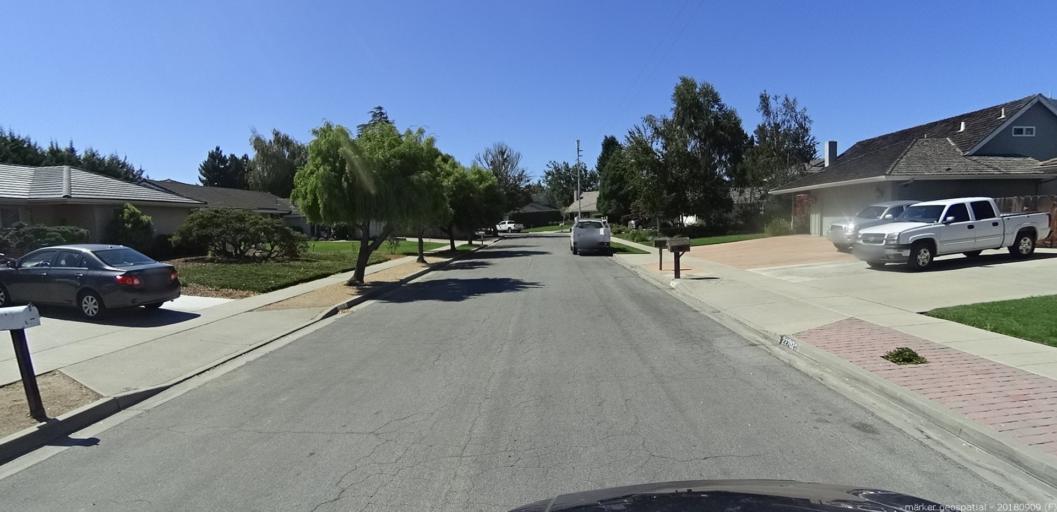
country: US
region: California
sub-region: Monterey County
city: Salinas
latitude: 36.6045
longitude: -121.6988
